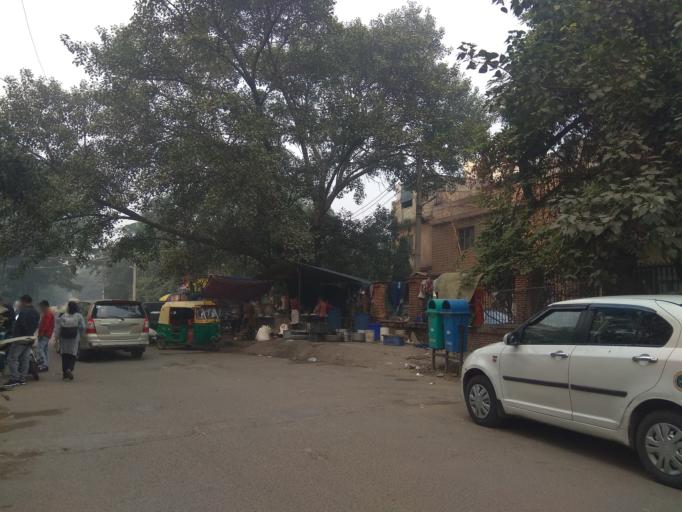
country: IN
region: NCT
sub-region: New Delhi
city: New Delhi
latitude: 28.5701
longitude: 77.2449
